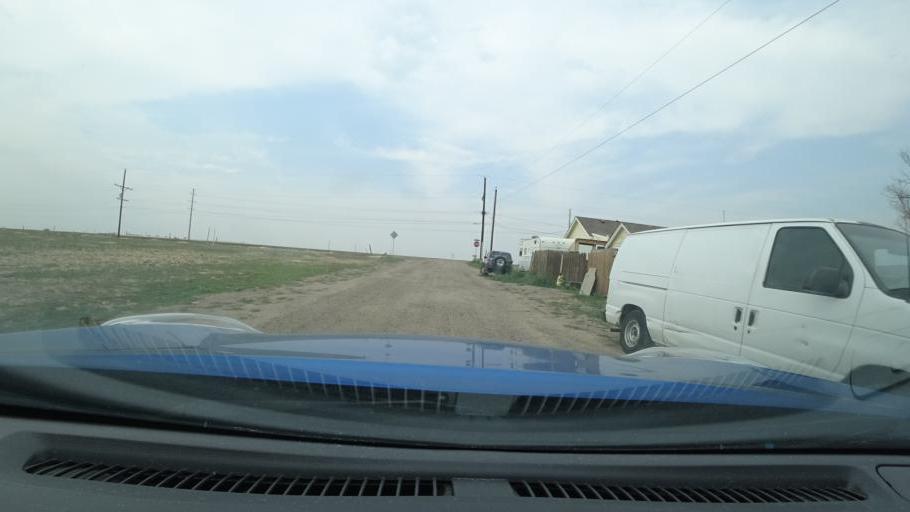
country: US
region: Colorado
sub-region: Adams County
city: Aurora
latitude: 39.7525
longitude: -104.7638
